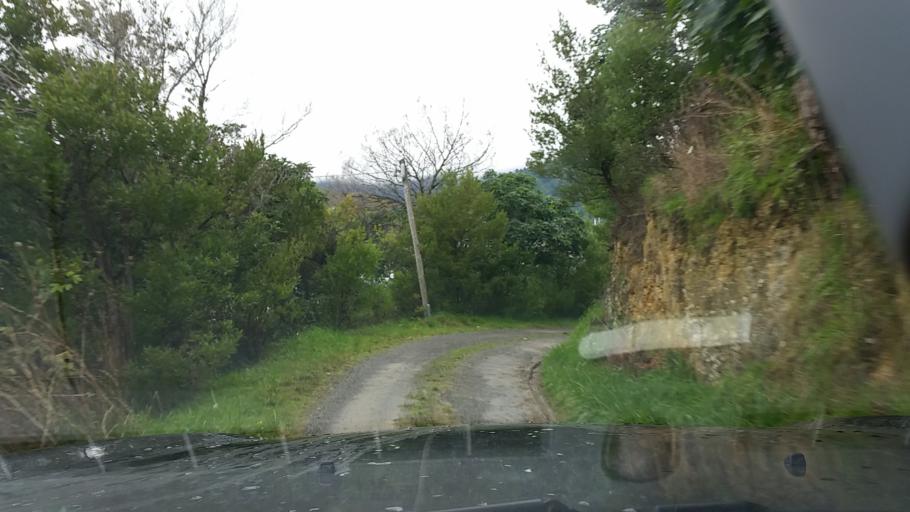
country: NZ
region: Marlborough
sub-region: Marlborough District
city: Picton
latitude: -41.2649
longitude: 174.0370
